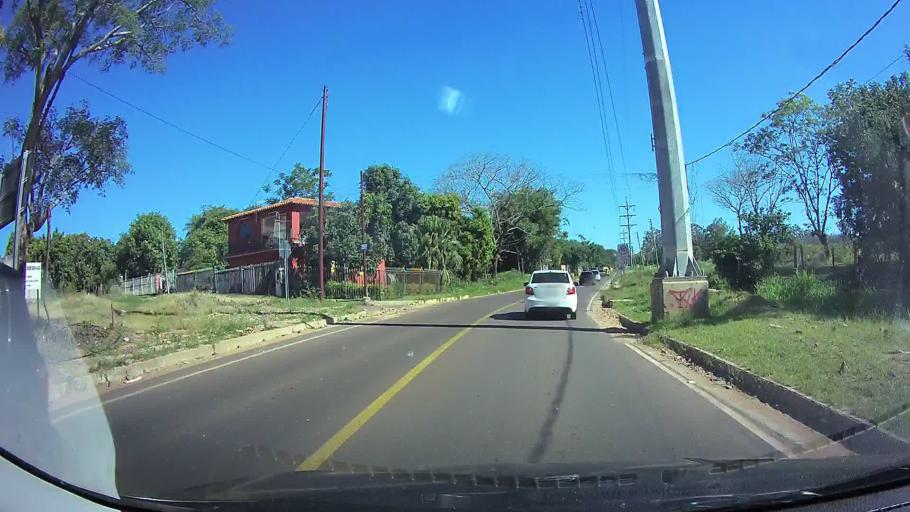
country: PY
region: Central
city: Fernando de la Mora
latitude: -25.2988
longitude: -57.5344
